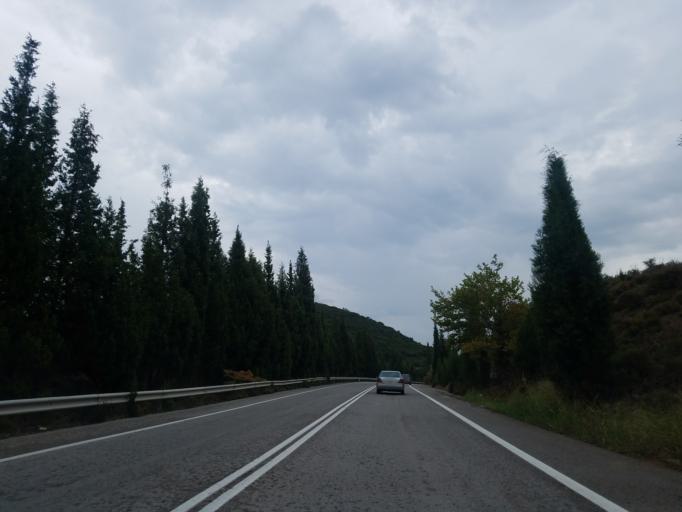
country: GR
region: Central Greece
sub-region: Nomos Voiotias
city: Livadeia
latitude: 38.4438
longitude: 22.8041
